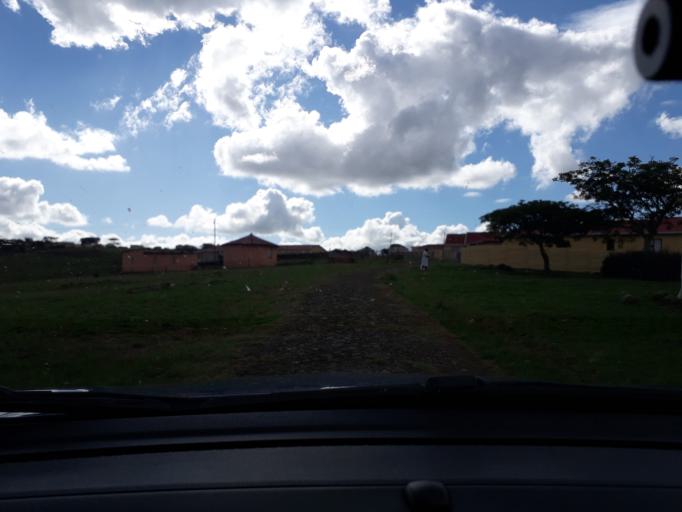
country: ZA
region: Eastern Cape
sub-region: Buffalo City Metropolitan Municipality
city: Bhisho
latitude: -33.1179
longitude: 27.4296
